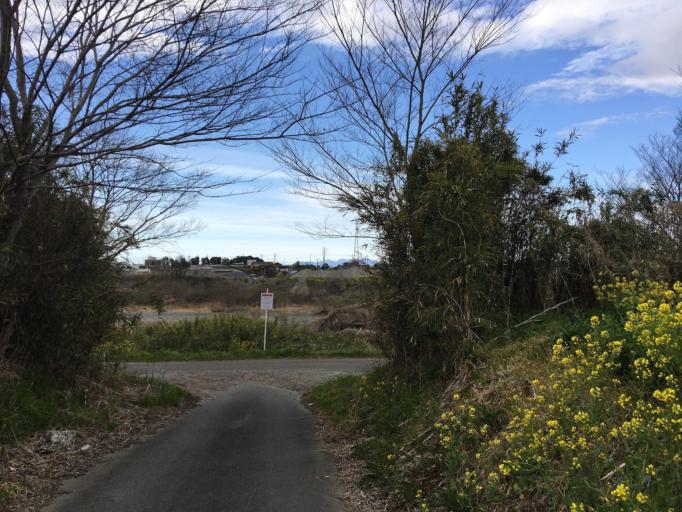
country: JP
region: Saitama
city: Yorii
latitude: 36.1168
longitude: 139.2491
